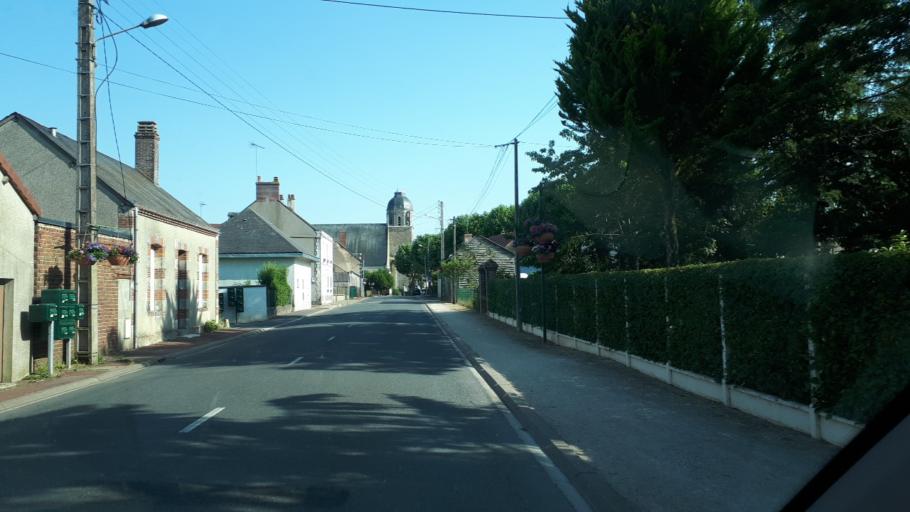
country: FR
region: Centre
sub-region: Departement du Loir-et-Cher
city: La Ville-aux-Clercs
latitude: 47.9204
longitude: 1.0848
